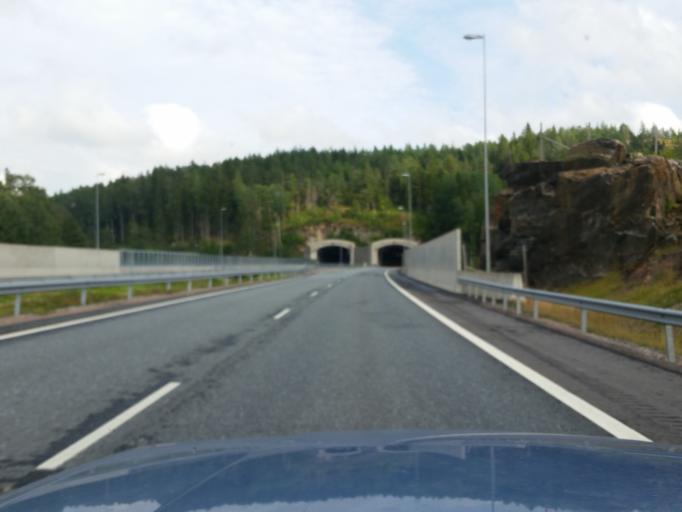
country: FI
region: Uusimaa
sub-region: Helsinki
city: Saukkola
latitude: 60.3126
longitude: 24.0012
